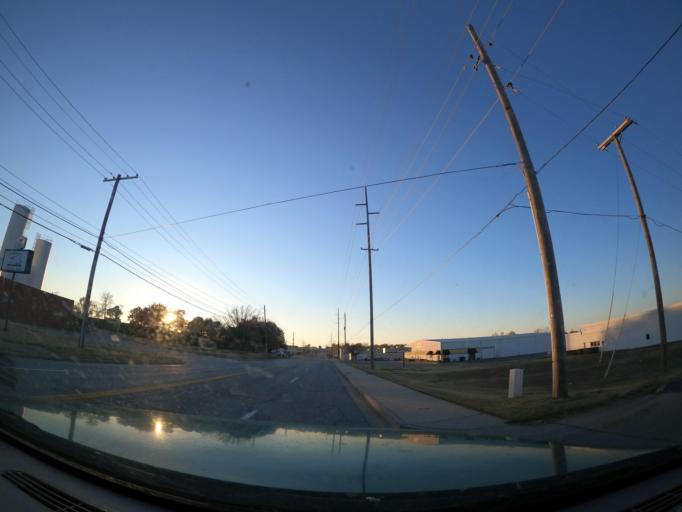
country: US
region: Oklahoma
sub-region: Tulsa County
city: Tulsa
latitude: 36.1407
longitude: -95.9070
